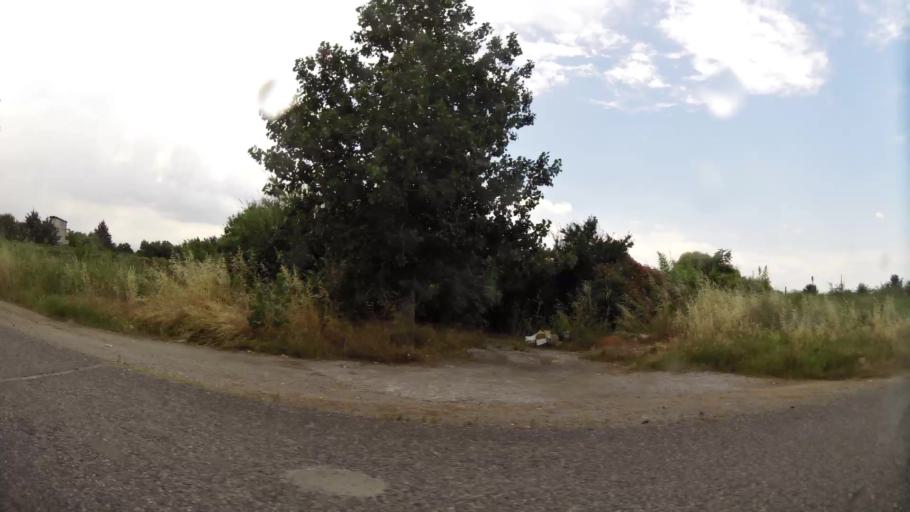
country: GR
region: Central Macedonia
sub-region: Nomos Pierias
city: Paralia
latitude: 40.2818
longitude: 22.6017
